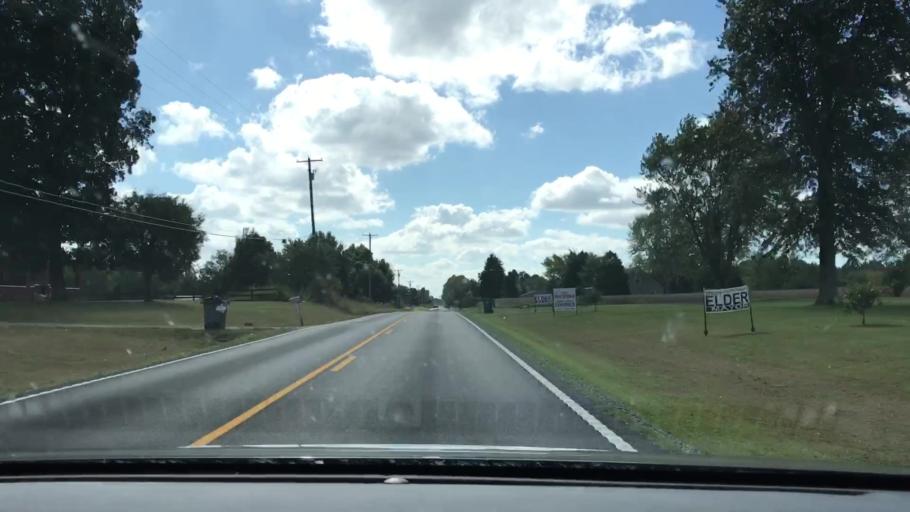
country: US
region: Kentucky
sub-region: Graves County
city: Mayfield
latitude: 36.8025
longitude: -88.5954
